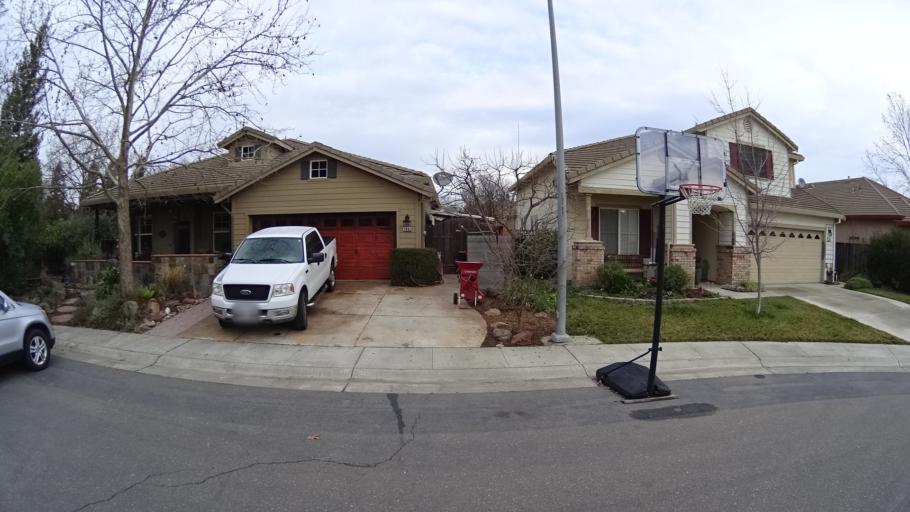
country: US
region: California
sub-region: Yolo County
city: Davis
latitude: 38.5666
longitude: -121.7263
